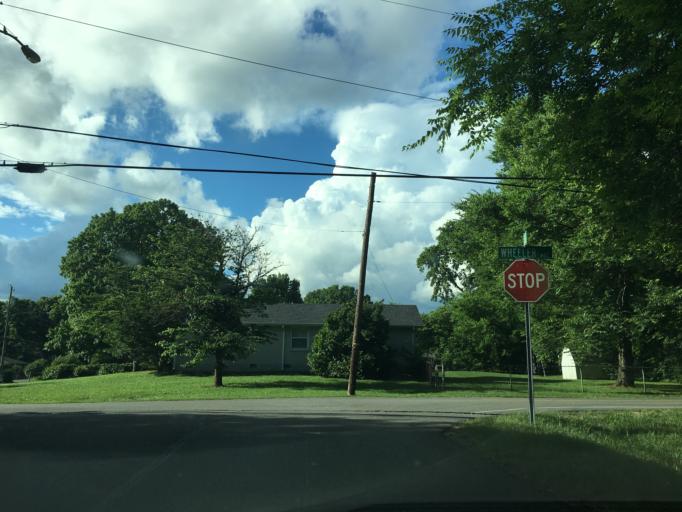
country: US
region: Tennessee
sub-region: Davidson County
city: Oak Hill
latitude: 36.0953
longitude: -86.7341
